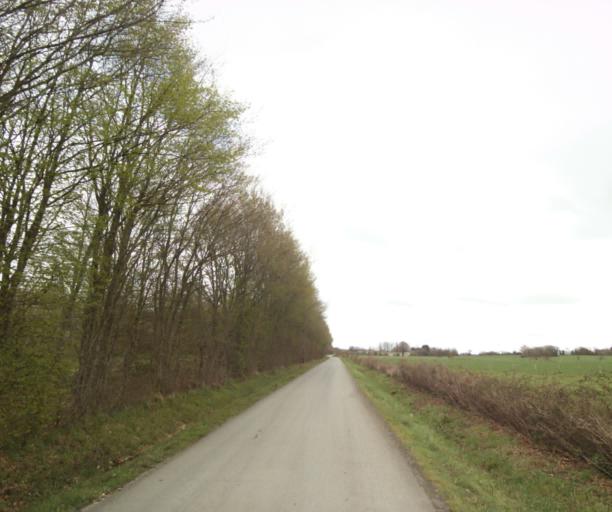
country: FR
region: Pays de la Loire
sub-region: Departement de la Loire-Atlantique
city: Bouvron
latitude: 47.4252
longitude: -1.8501
